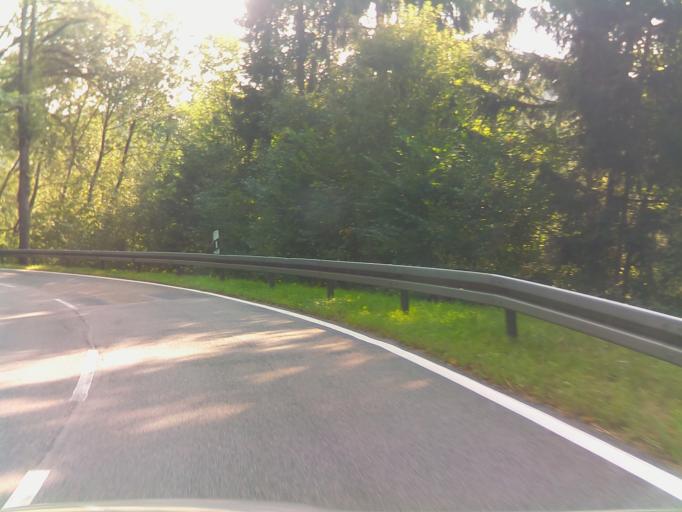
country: DE
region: Hesse
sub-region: Regierungsbezirk Darmstadt
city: Rothenberg
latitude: 49.5474
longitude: 8.9291
